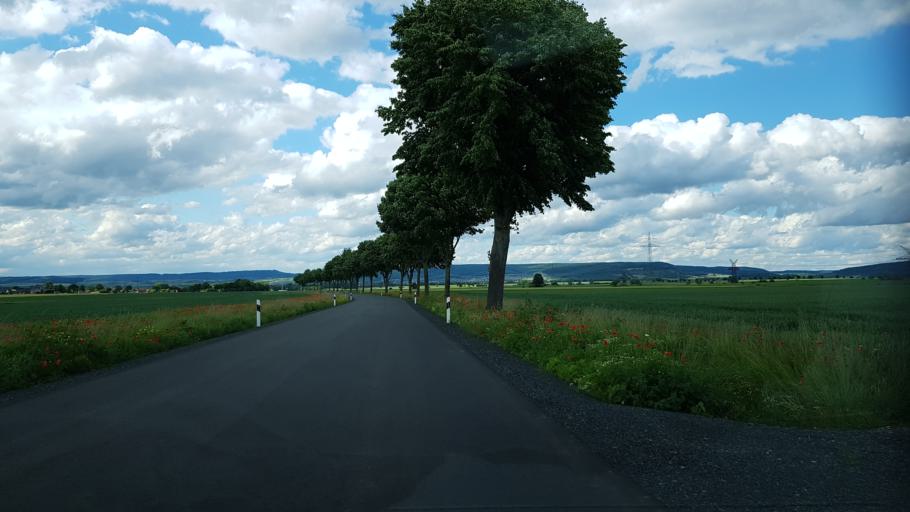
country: DE
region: Lower Saxony
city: Moringen
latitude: 51.7552
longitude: 9.8728
